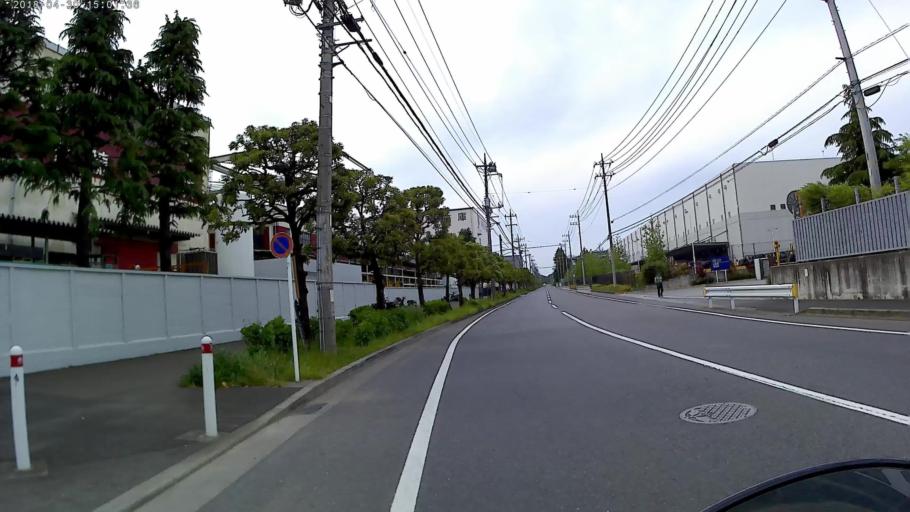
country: JP
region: Kanagawa
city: Zama
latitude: 35.5559
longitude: 139.3438
